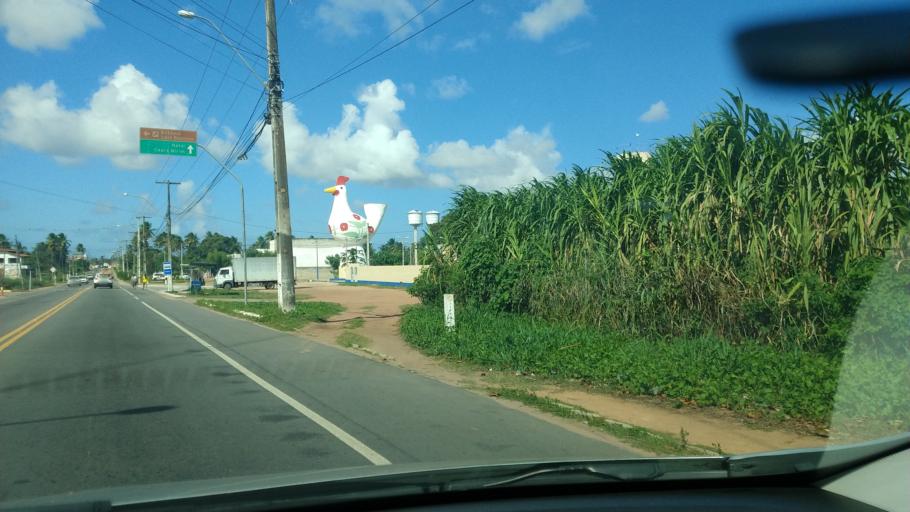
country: BR
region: Rio Grande do Norte
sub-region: Sao Goncalo Do Amarante
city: Sao Goncalo do Amarante
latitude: -5.7892
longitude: -35.3039
